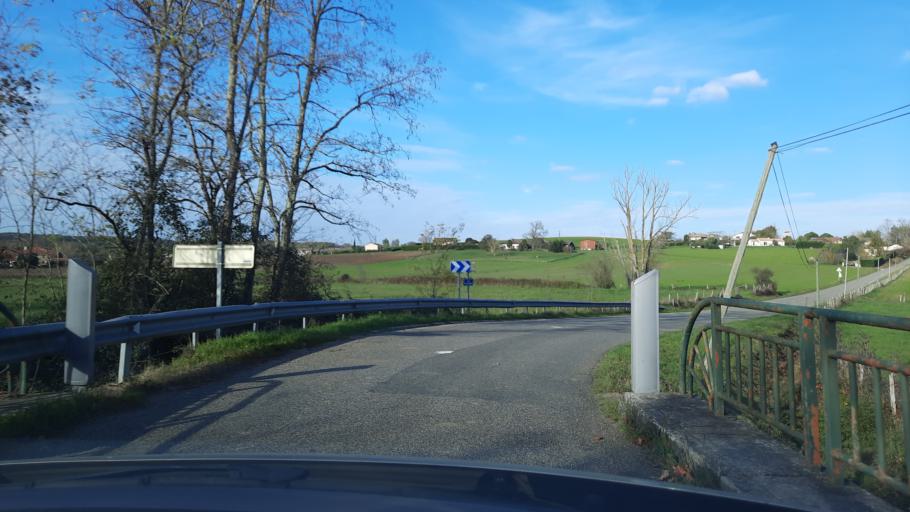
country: FR
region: Midi-Pyrenees
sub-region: Departement du Tarn-et-Garonne
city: Lafrancaise
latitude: 44.1617
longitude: 1.2647
